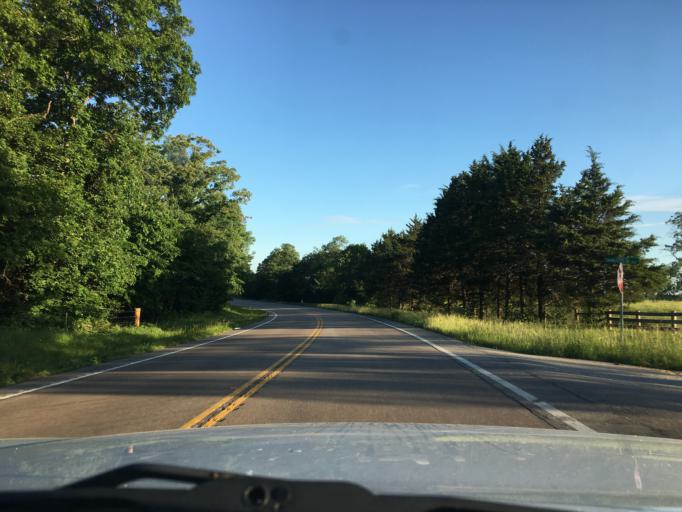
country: US
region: Missouri
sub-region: Gasconade County
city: Owensville
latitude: 38.4502
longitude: -91.4478
